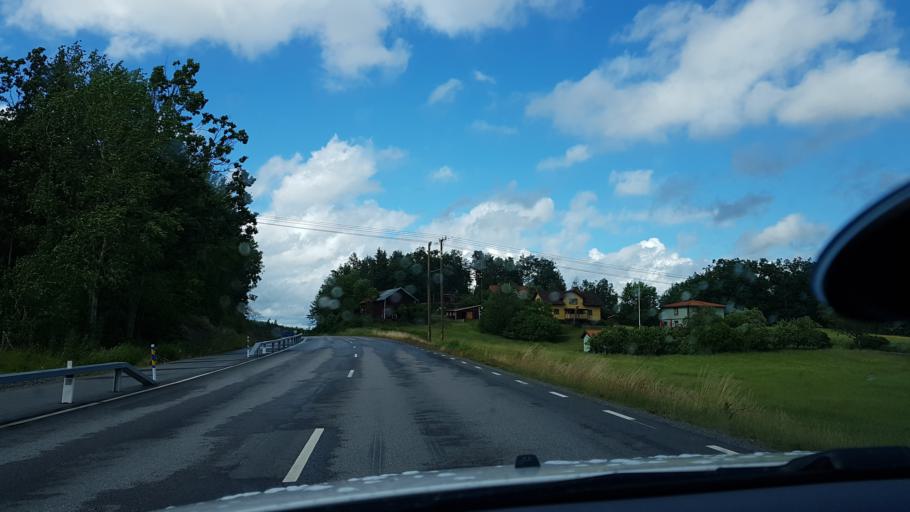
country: SE
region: OEstergoetland
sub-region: Valdemarsviks Kommun
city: Gusum
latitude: 58.2776
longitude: 16.5060
